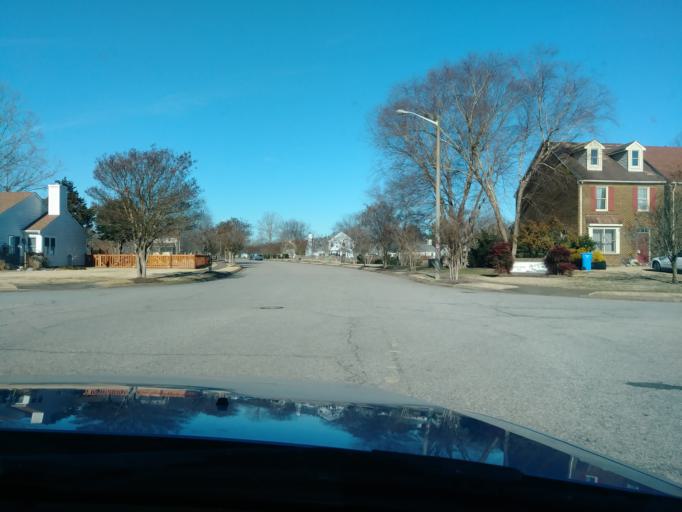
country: US
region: Virginia
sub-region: City of Chesapeake
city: Chesapeake
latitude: 36.7553
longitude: -76.2085
